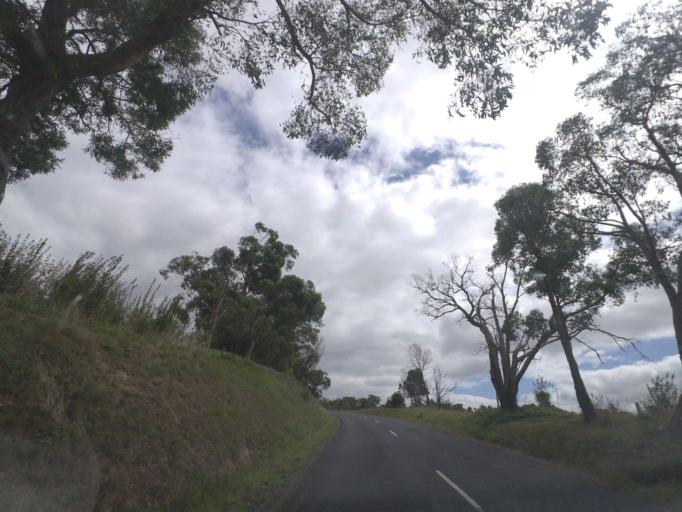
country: AU
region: Victoria
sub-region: Yarra Ranges
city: Woori Yallock
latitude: -37.8096
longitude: 145.5036
